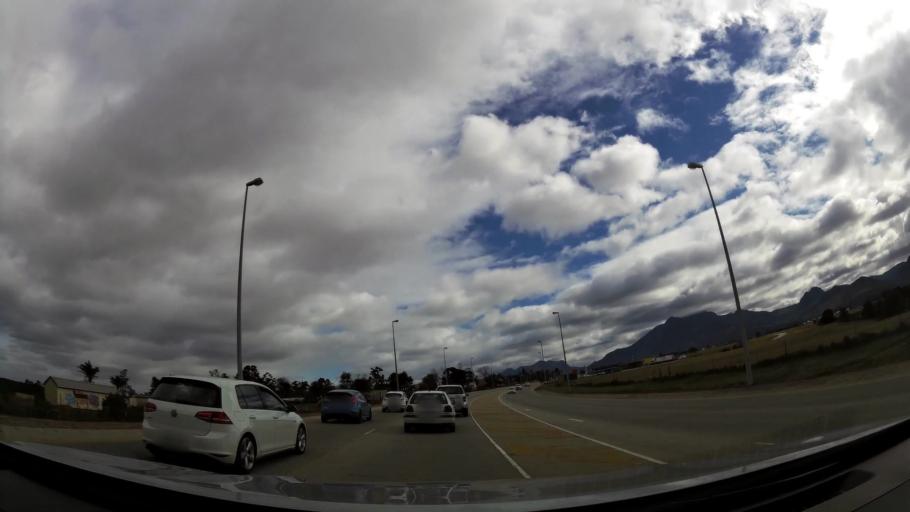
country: ZA
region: Western Cape
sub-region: Eden District Municipality
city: George
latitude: -33.9944
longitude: 22.5227
